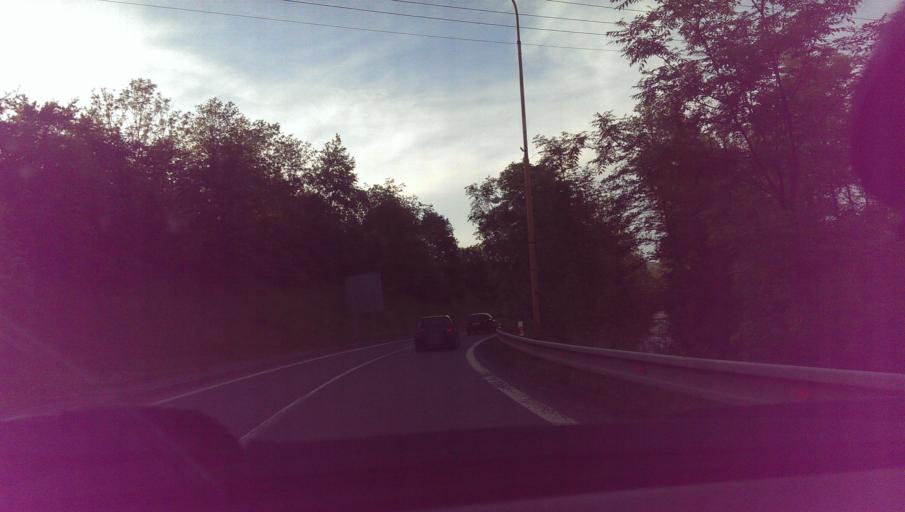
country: CZ
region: Zlin
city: Valasska Polanka
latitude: 49.2535
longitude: 17.9978
